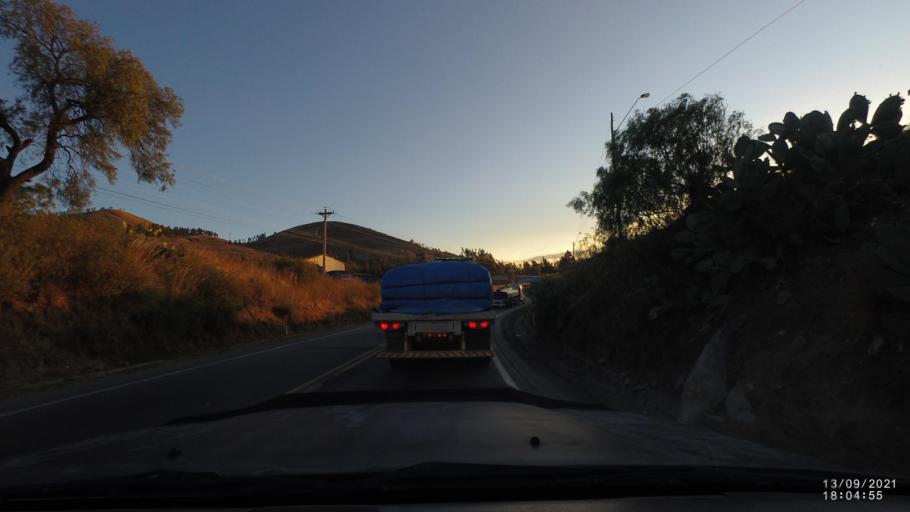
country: BO
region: Cochabamba
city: Colomi
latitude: -17.4195
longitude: -65.9422
